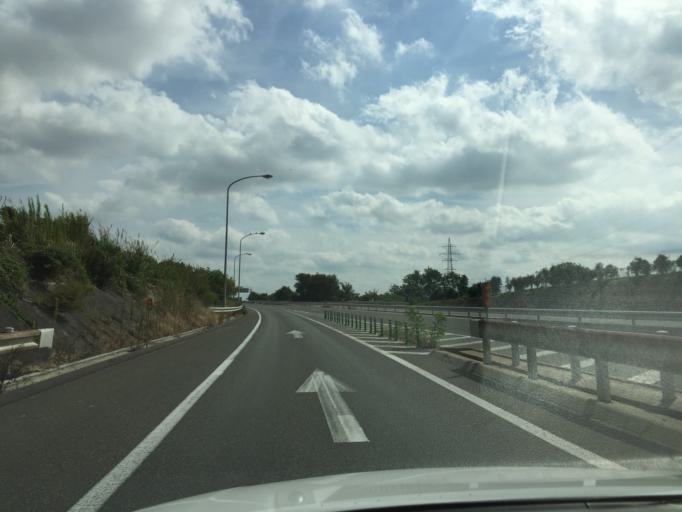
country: JP
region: Fukushima
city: Motomiya
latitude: 37.4645
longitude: 140.3564
